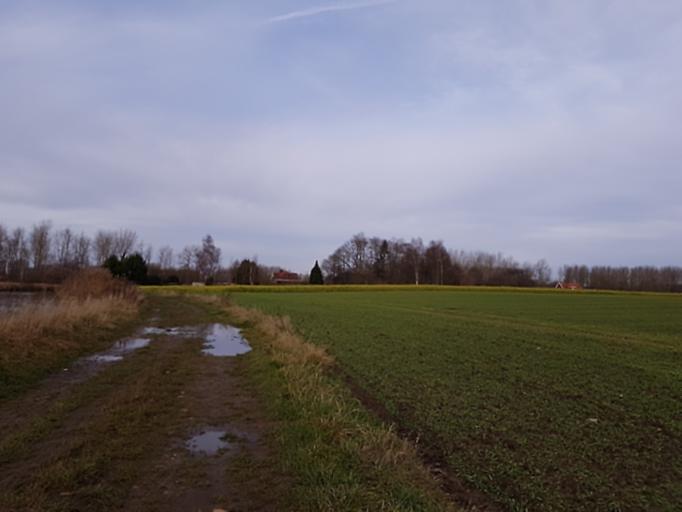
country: BE
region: Flanders
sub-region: Provincie Vlaams-Brabant
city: Rotselaar
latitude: 50.9367
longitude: 4.7121
